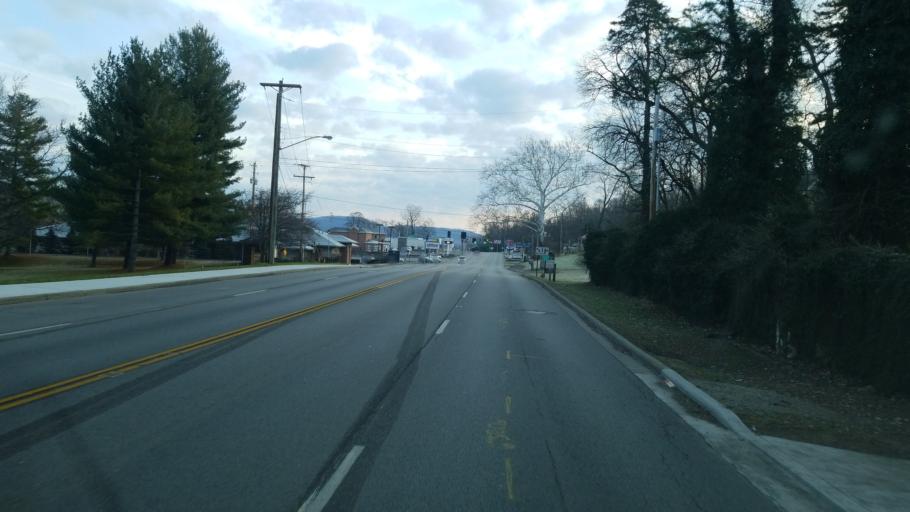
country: US
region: Ohio
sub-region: Ross County
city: North Fork Village
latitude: 39.3330
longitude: -83.0091
